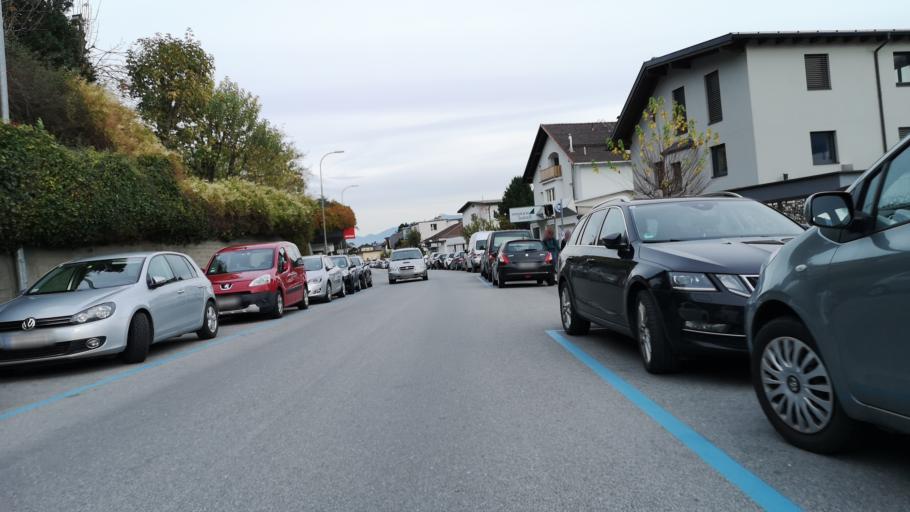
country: AT
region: Tyrol
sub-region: Innsbruck Stadt
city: Innsbruck
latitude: 47.2688
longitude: 11.3764
